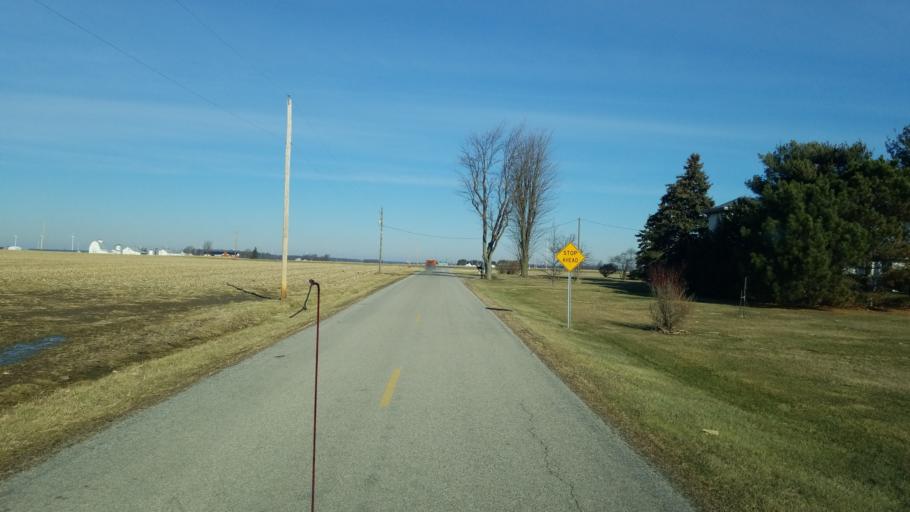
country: US
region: Ohio
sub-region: Hardin County
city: Kenton
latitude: 40.7299
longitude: -83.6913
